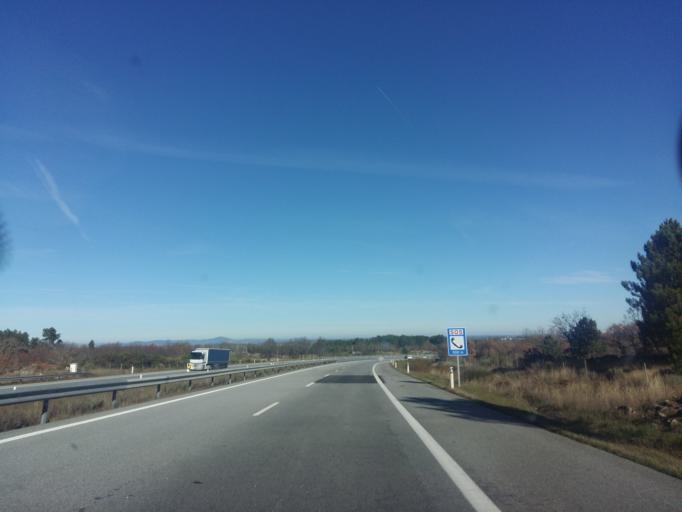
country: PT
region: Guarda
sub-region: Guarda
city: Sequeira
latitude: 40.5974
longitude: -7.1317
